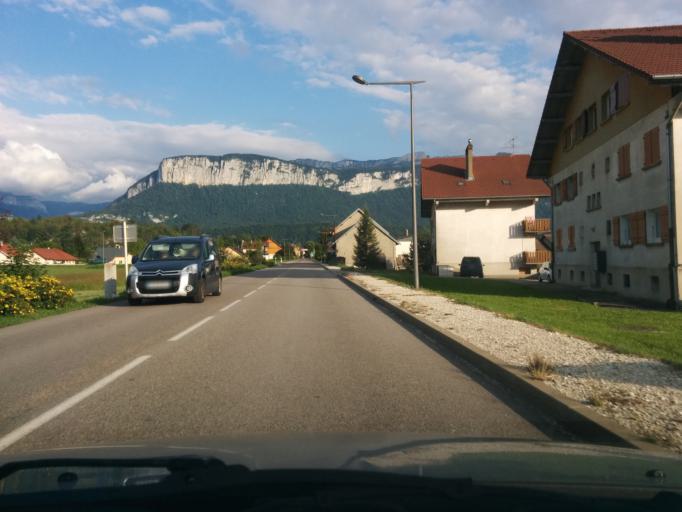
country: FR
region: Rhone-Alpes
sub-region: Departement de la Savoie
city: Les Echelles
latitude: 45.4425
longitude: 5.7447
